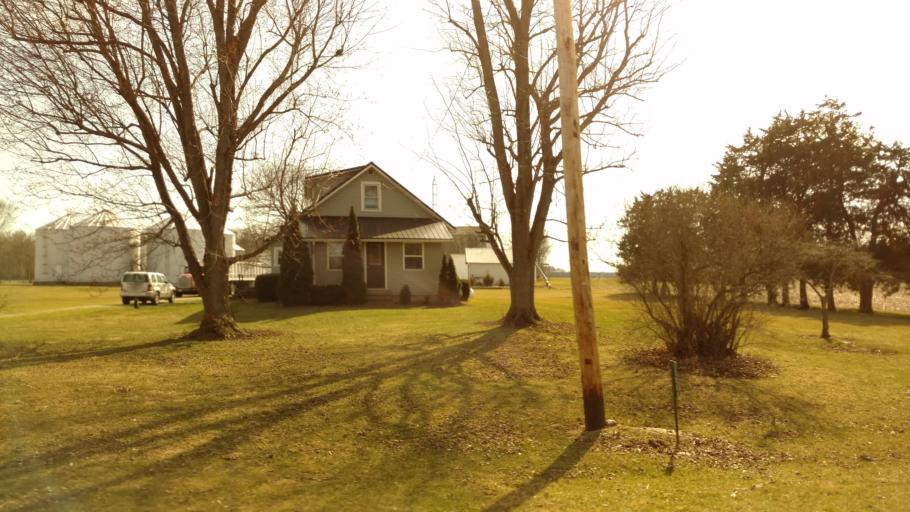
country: US
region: Ohio
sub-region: Hardin County
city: Kenton
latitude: 40.5860
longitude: -83.4861
